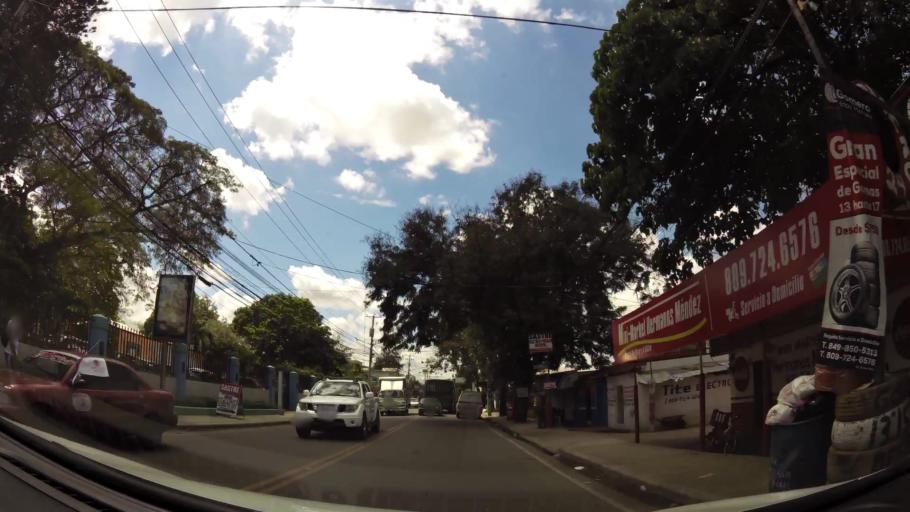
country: DO
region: Santiago
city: Santiago de los Caballeros
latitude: 19.4746
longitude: -70.6771
